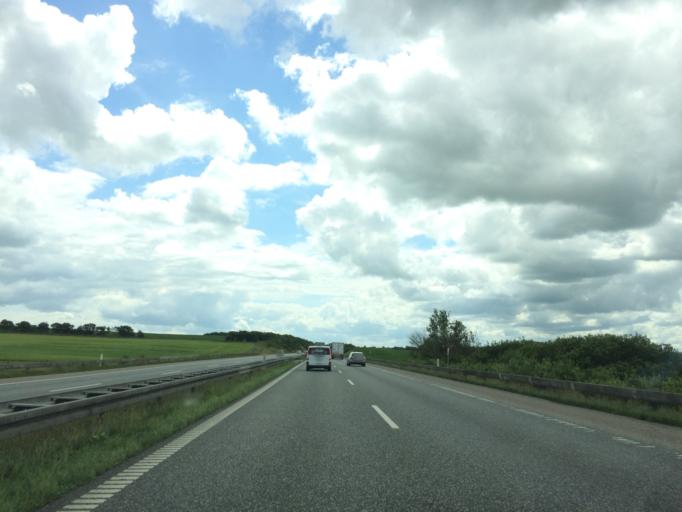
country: DK
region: North Denmark
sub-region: Rebild Kommune
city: Stovring
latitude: 56.8078
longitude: 9.7130
